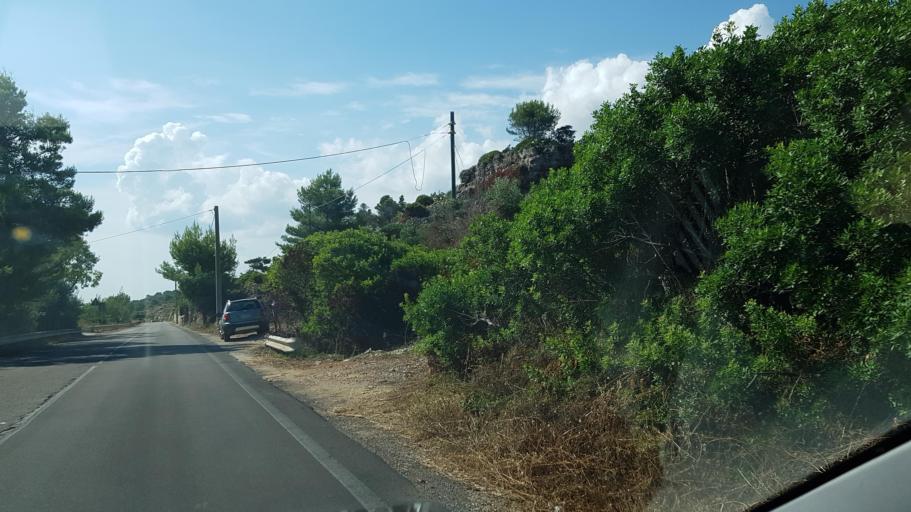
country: IT
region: Apulia
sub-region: Provincia di Lecce
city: Morciano di Leuca
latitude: 39.8166
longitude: 18.3100
